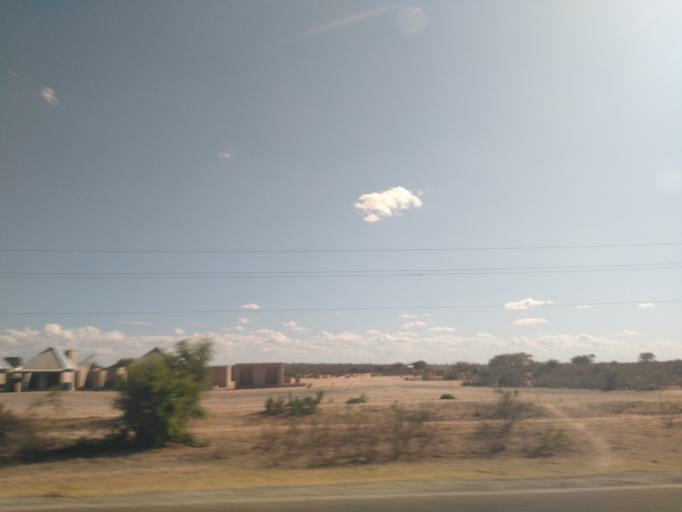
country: TZ
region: Dodoma
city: Dodoma
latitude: -6.1417
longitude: 35.6946
